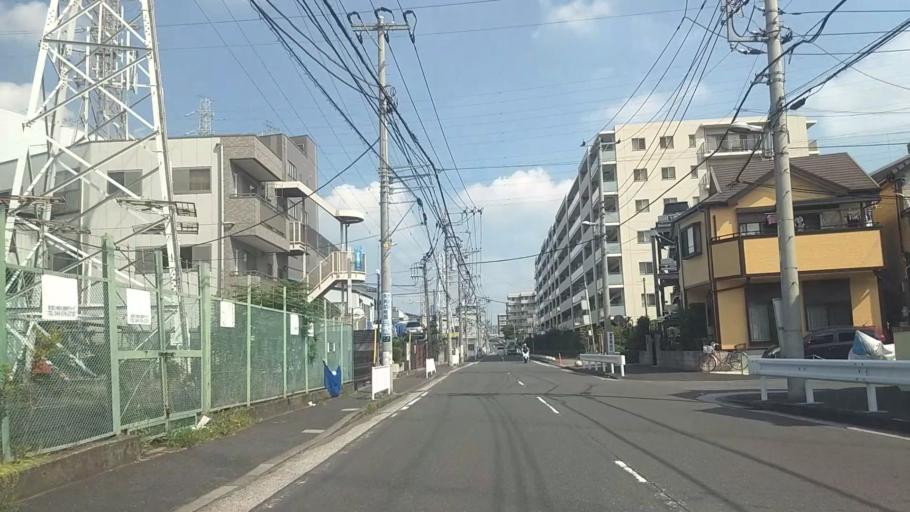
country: JP
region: Kanagawa
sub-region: Kawasaki-shi
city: Kawasaki
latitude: 35.5265
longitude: 139.6789
